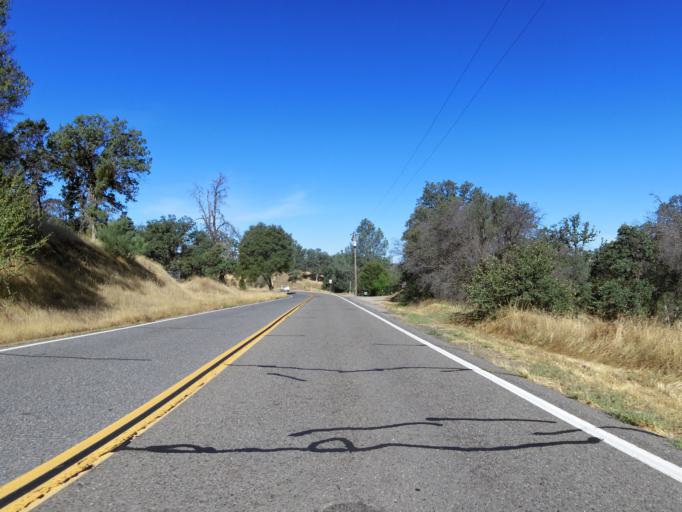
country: US
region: California
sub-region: Madera County
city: Yosemite Lakes
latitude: 37.2266
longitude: -119.7658
